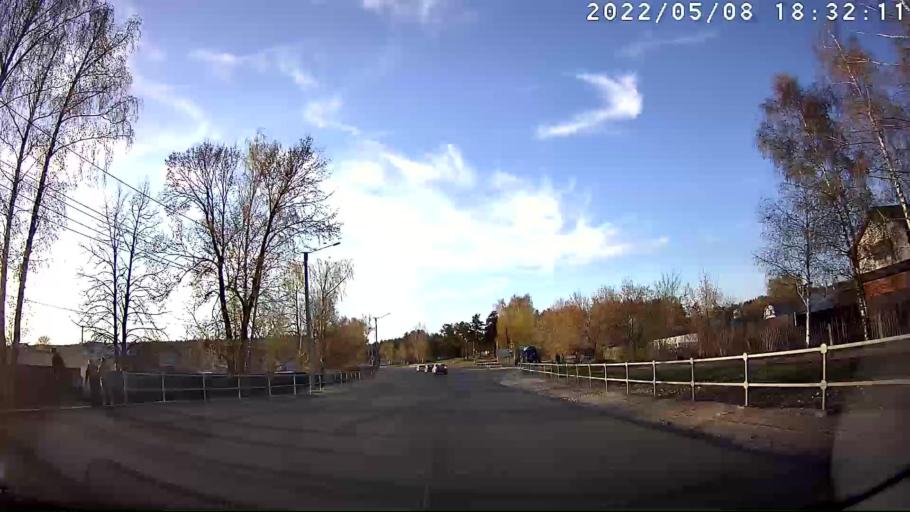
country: RU
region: Mariy-El
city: Volzhsk
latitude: 55.8858
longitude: 48.3597
